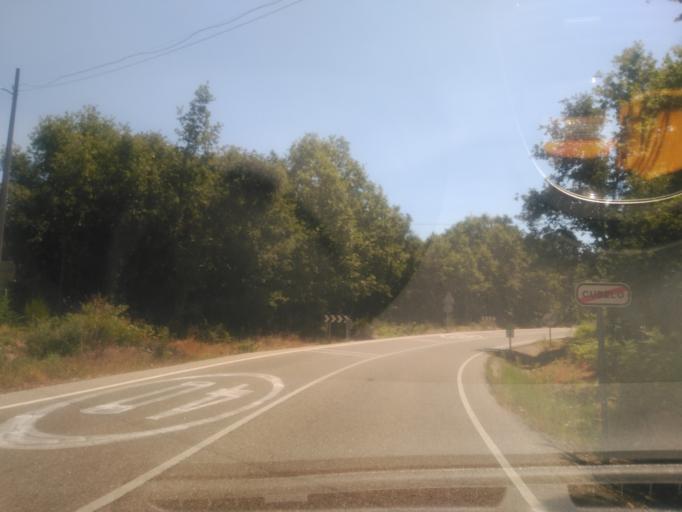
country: ES
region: Castille and Leon
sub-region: Provincia de Zamora
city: Galende
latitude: 42.0970
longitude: -6.6485
